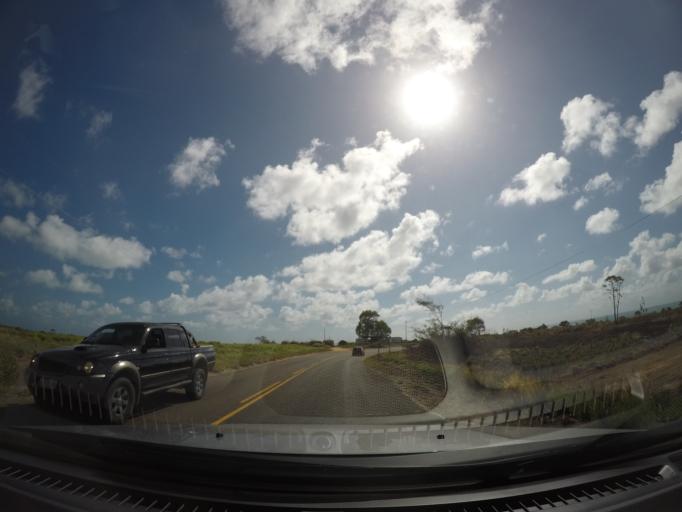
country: BR
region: Paraiba
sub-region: Pitimbu
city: Pitimbu
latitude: -7.3922
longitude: -34.8153
